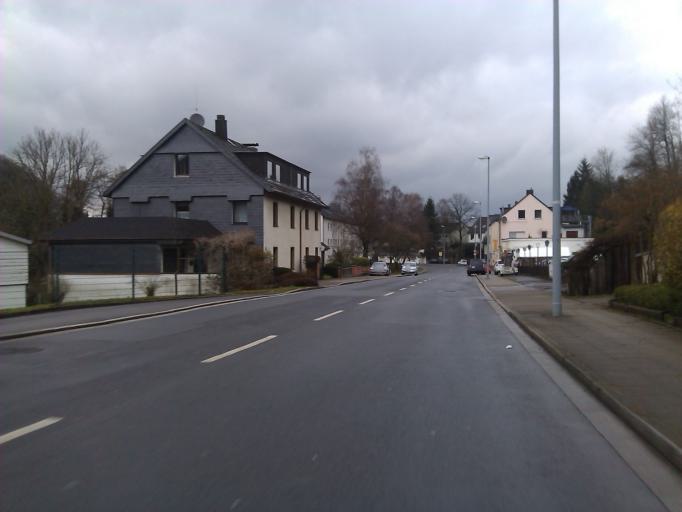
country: DE
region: North Rhine-Westphalia
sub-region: Regierungsbezirk Dusseldorf
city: Heiligenhaus
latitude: 51.3526
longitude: 6.9312
